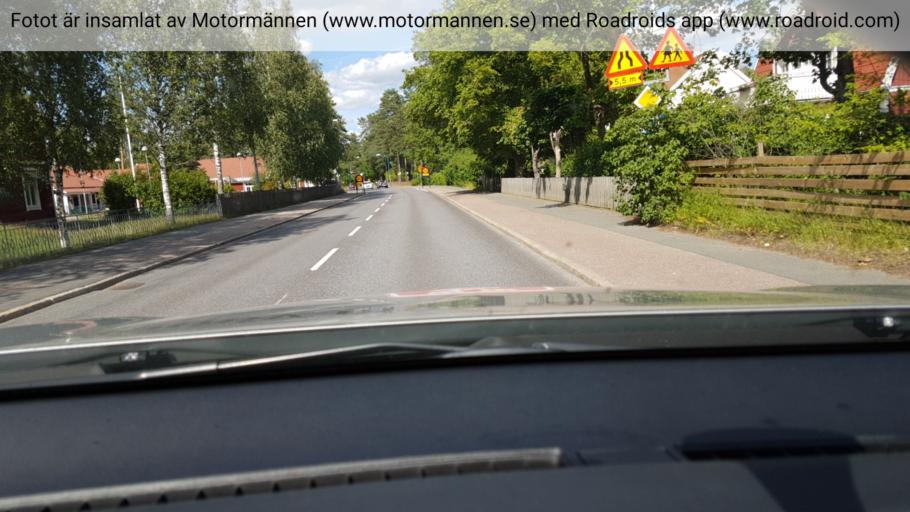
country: SE
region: Joenkoeping
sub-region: Vaggeryds Kommun
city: Vaggeryd
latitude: 57.4916
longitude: 14.1289
